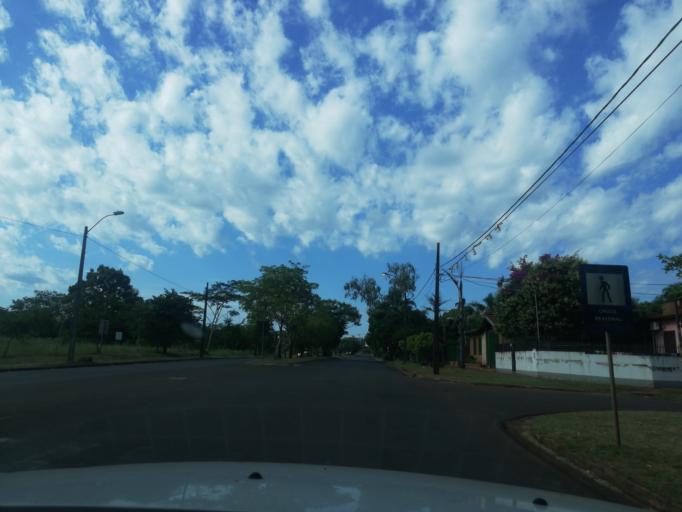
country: PY
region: Itapua
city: Encarnacion
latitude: -27.3498
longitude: -55.8490
